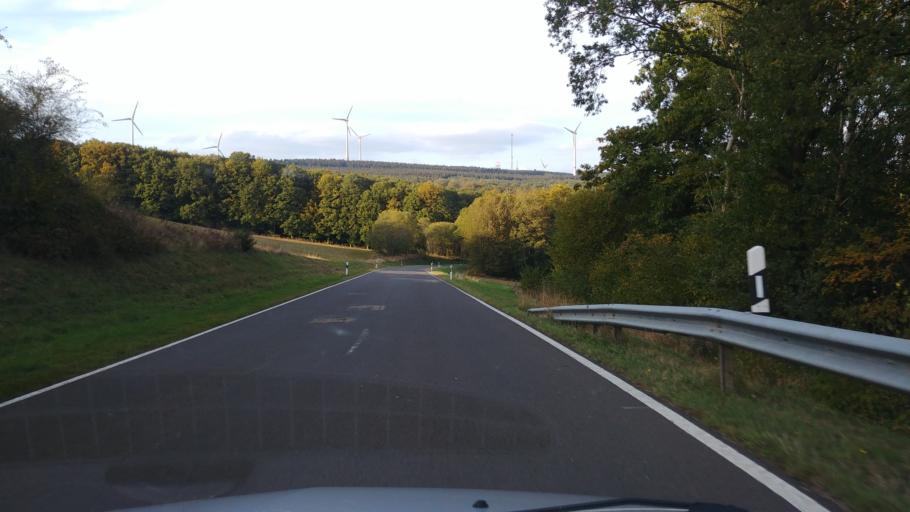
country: DE
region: Rheinland-Pfalz
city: Gornhausen
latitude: 49.8217
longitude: 7.0480
